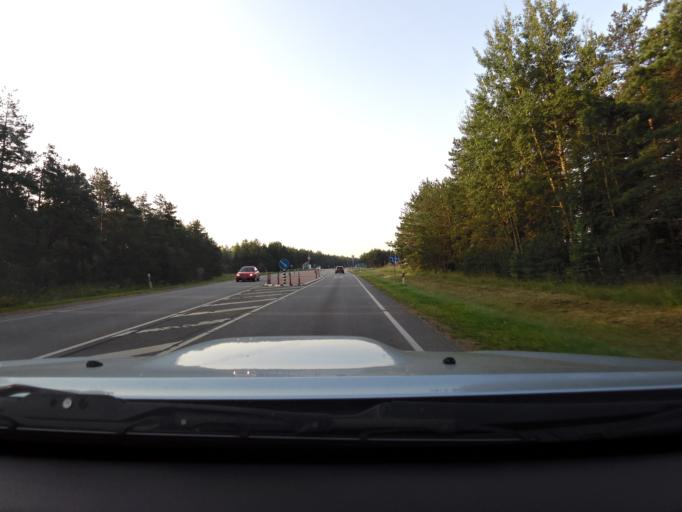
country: LT
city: Trakai
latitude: 54.5040
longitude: 24.9891
